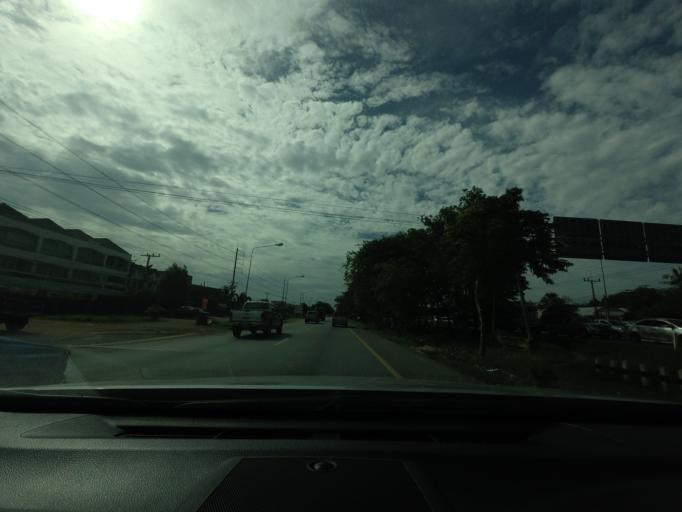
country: TH
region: Songkhla
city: Hat Yai
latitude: 6.9943
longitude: 100.4179
